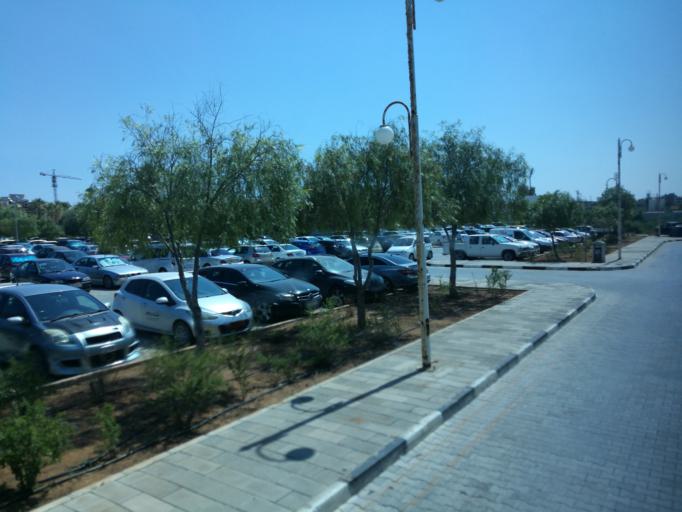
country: CY
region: Ammochostos
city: Famagusta
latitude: 35.1202
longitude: 33.9567
